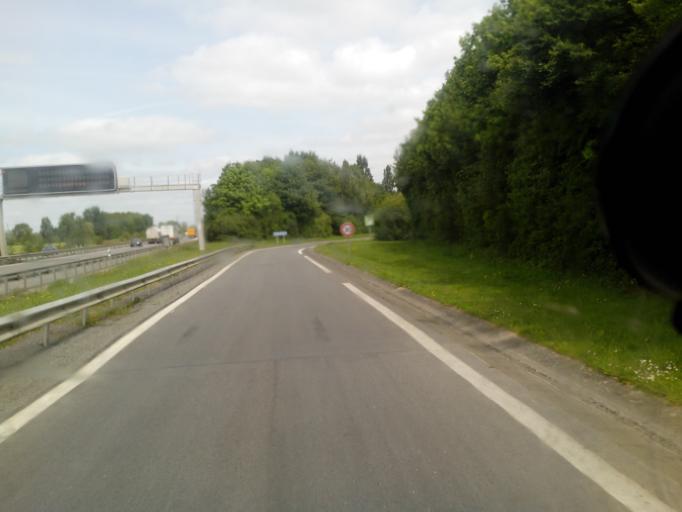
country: FR
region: Brittany
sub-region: Departement d'Ille-et-Vilaine
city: Chatillon-sur-Seiche
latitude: 48.0568
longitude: -1.6803
